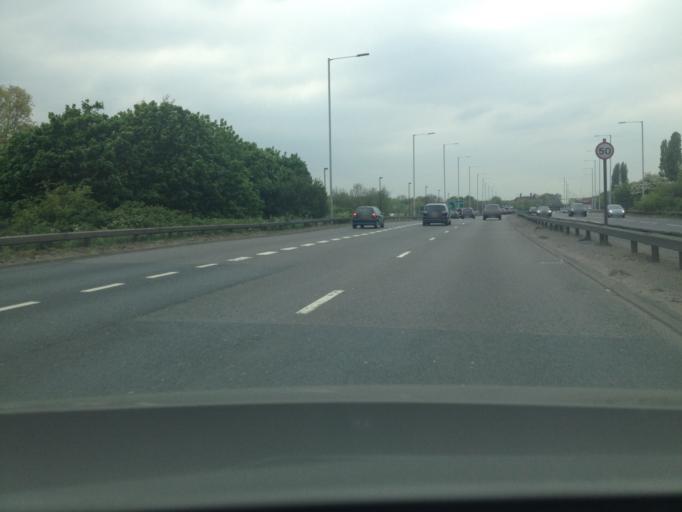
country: GB
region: England
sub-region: Greater London
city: Northolt
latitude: 51.5404
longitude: -0.3700
